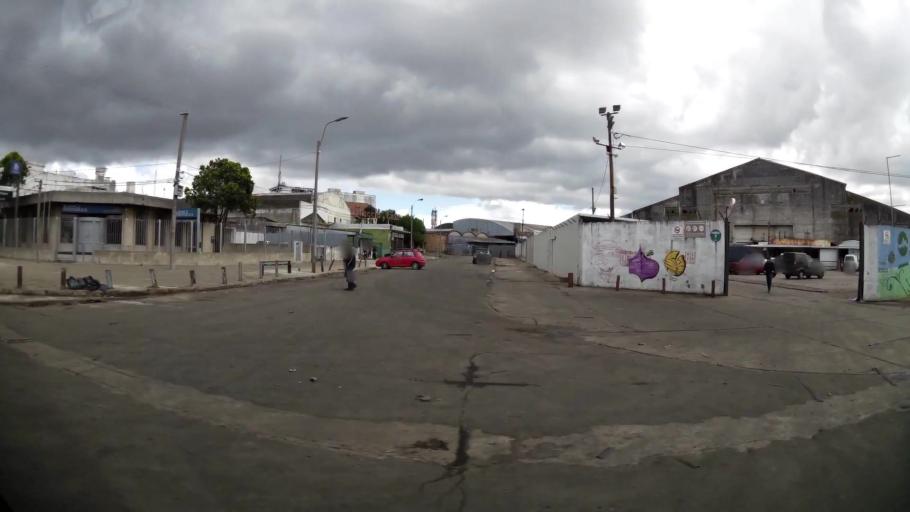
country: UY
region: Montevideo
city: Montevideo
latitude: -34.8732
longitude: -56.1525
